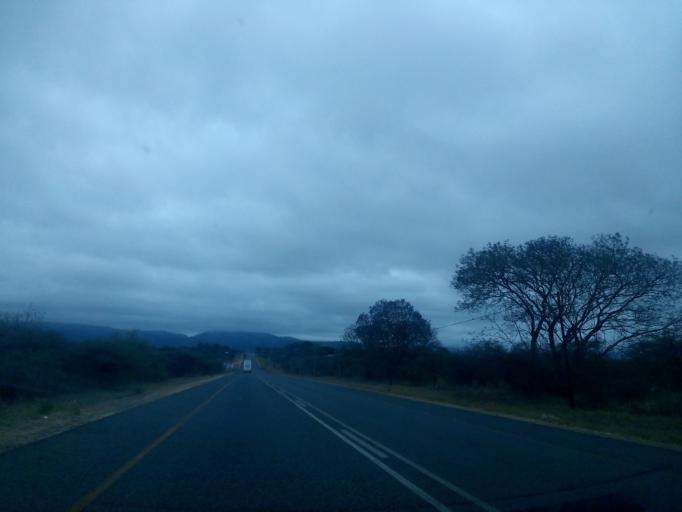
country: ZA
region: Limpopo
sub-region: Vhembe District Municipality
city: Louis Trichardt
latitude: -23.0865
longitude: 29.9059
